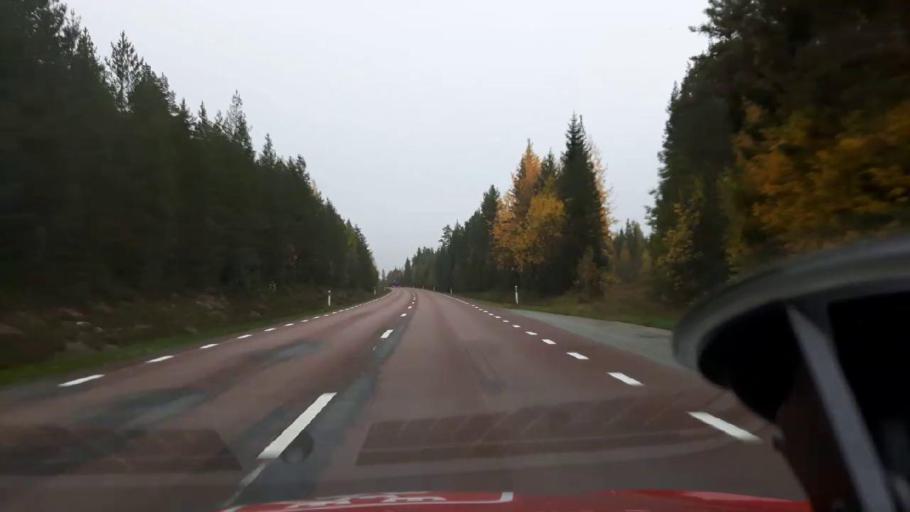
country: SE
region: Jaemtland
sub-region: Bergs Kommun
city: Hoverberg
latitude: 62.6074
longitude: 14.4036
